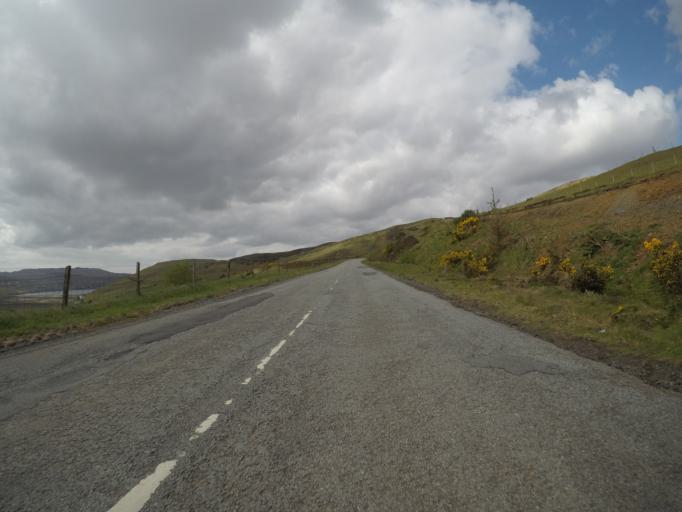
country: GB
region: Scotland
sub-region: Highland
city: Isle of Skye
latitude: 57.3021
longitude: -6.2978
